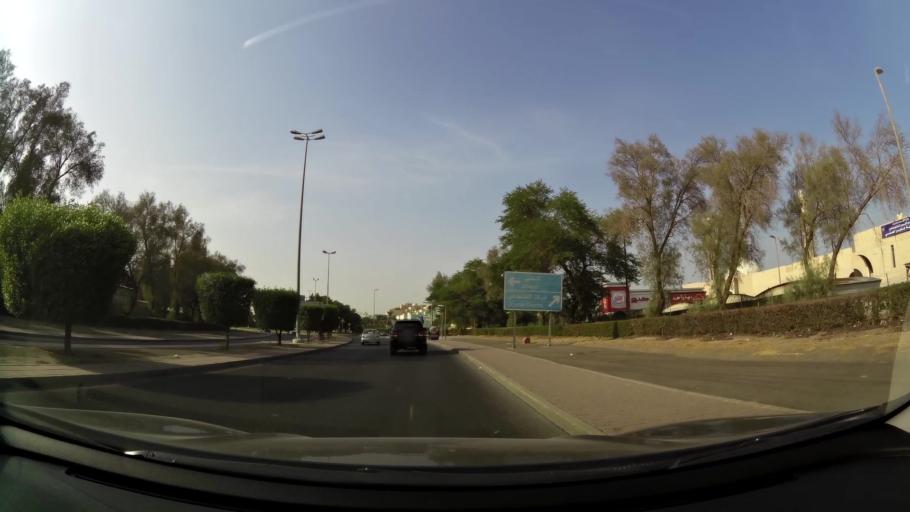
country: KW
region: Mubarak al Kabir
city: Mubarak al Kabir
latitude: 29.1721
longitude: 48.0779
